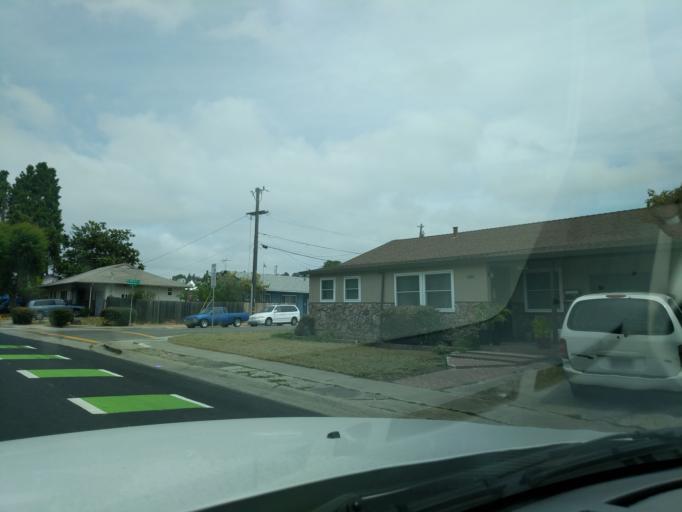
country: US
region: California
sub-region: Alameda County
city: Hayward
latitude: 37.6402
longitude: -122.0647
